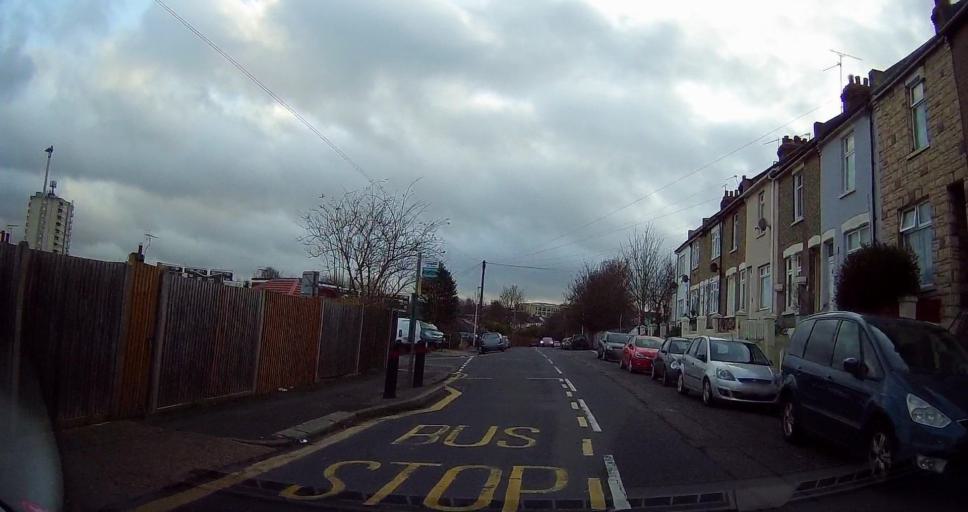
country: GB
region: England
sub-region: Kent
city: Chatham
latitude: 51.3723
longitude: 0.5328
